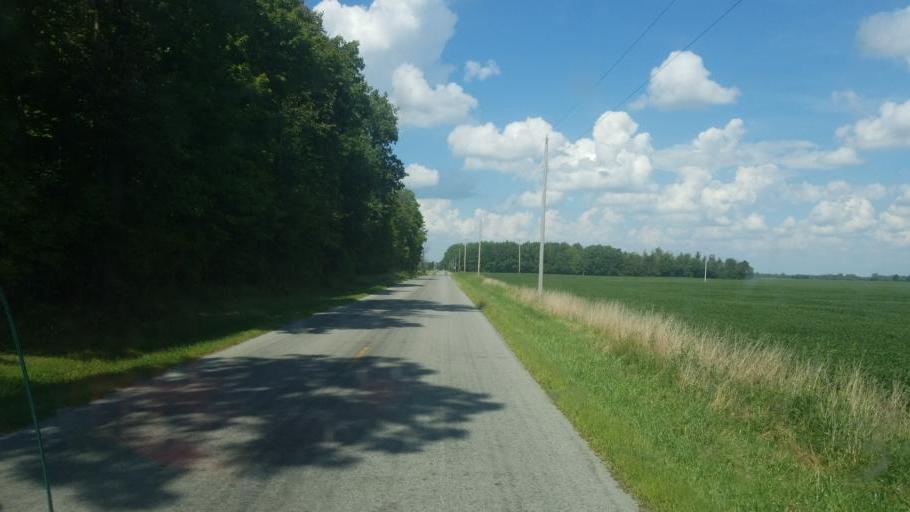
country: US
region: Ohio
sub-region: Wyandot County
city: Carey
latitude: 40.8736
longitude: -83.4192
